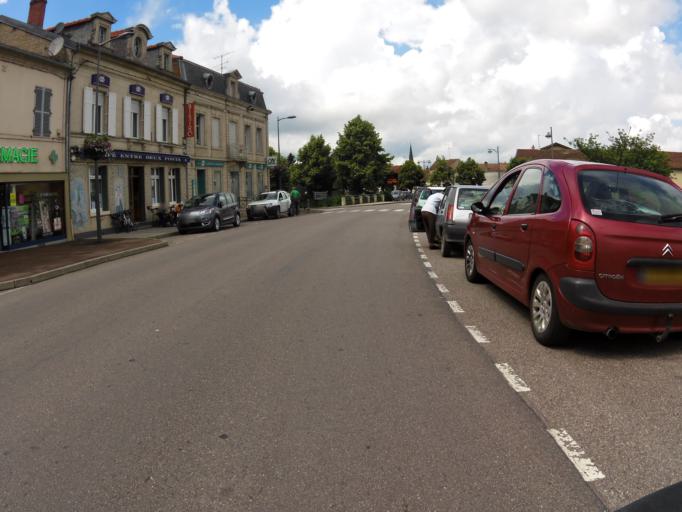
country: FR
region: Lorraine
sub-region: Departement de la Meuse
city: Revigny-sur-Ornain
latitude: 48.8264
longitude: 4.9849
